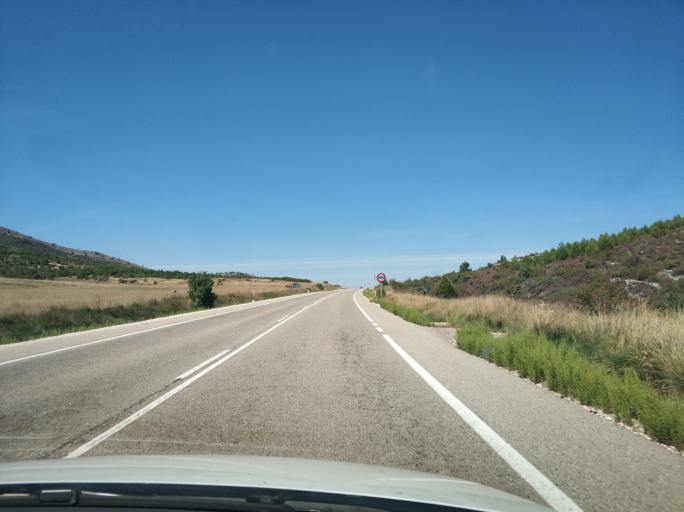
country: ES
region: Castille and Leon
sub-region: Provincia de Burgos
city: Covarrubias
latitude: 42.1056
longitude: -3.5098
